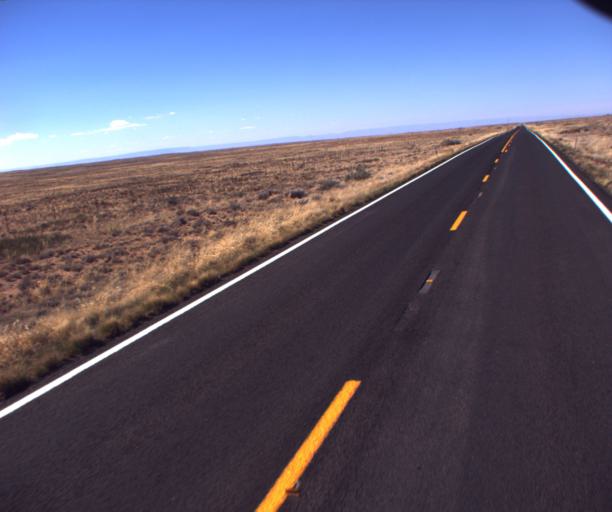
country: US
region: Arizona
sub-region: Coconino County
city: Tuba City
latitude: 35.9698
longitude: -110.9611
